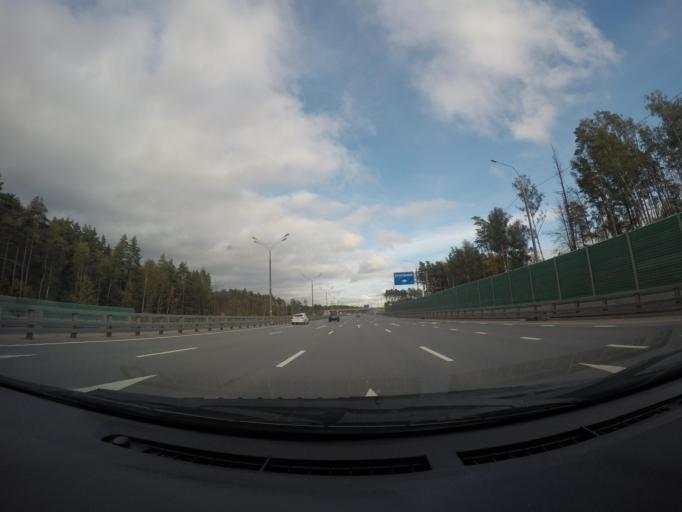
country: RU
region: Moskovskaya
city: Zhavoronki
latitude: 55.6150
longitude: 37.0902
